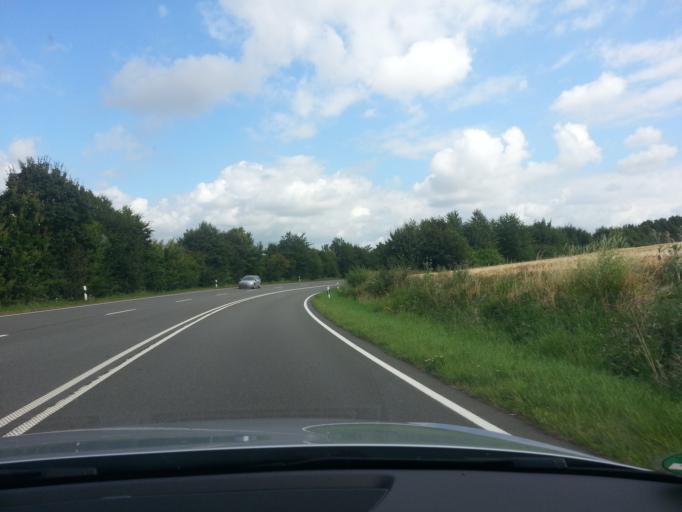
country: DE
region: Rheinland-Pfalz
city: Kirf
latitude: 49.5289
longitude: 6.4354
